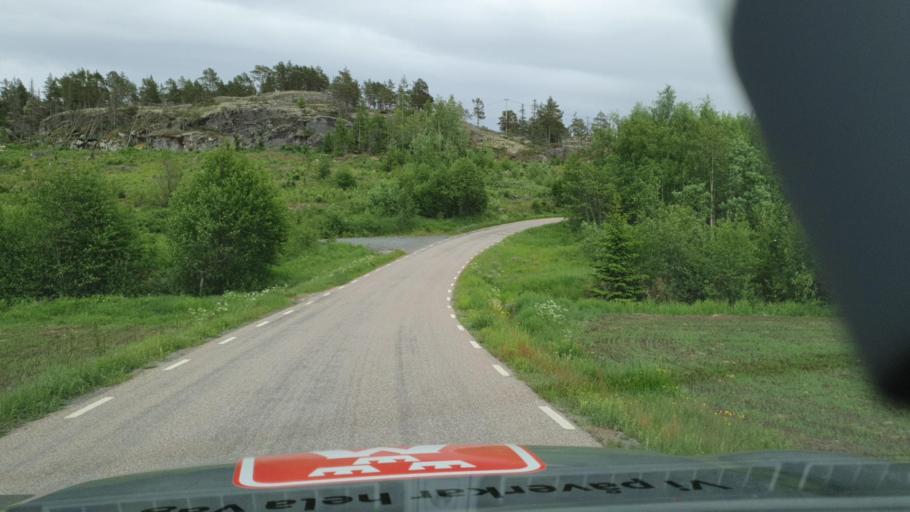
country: SE
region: Vaesternorrland
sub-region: Kramfors Kommun
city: Nordingra
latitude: 62.8798
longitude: 18.4299
